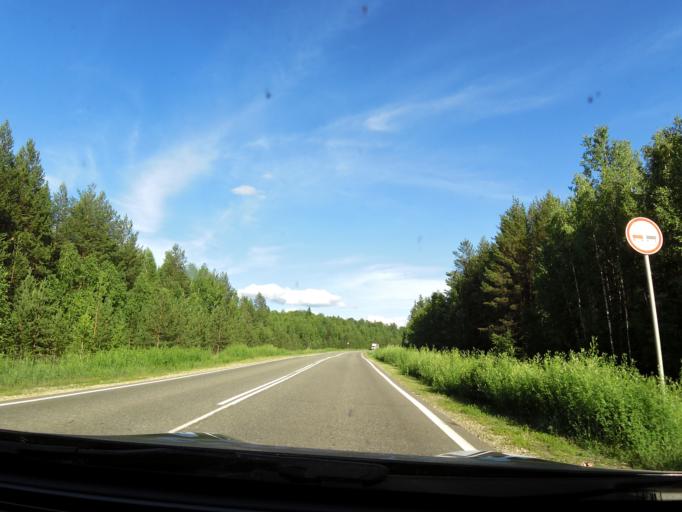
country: RU
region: Kirov
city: Chernaya Kholunitsa
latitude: 58.8220
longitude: 51.8039
